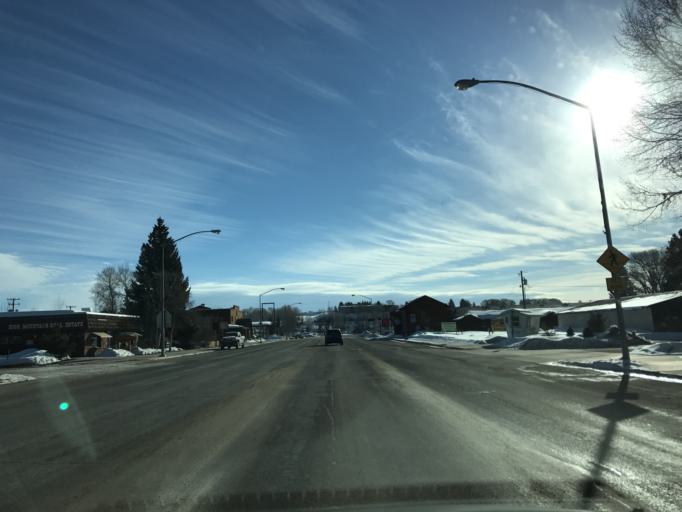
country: US
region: Wyoming
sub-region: Sublette County
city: Pinedale
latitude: 42.8666
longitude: -109.8604
